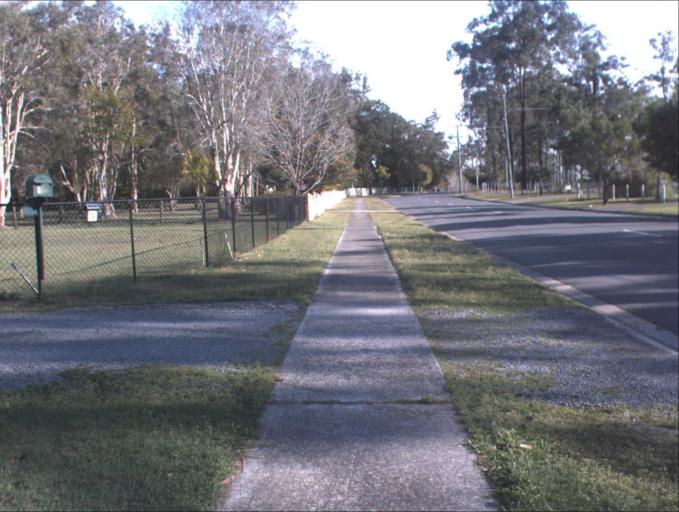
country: AU
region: Queensland
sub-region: Logan
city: Park Ridge South
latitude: -27.7001
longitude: 153.0269
